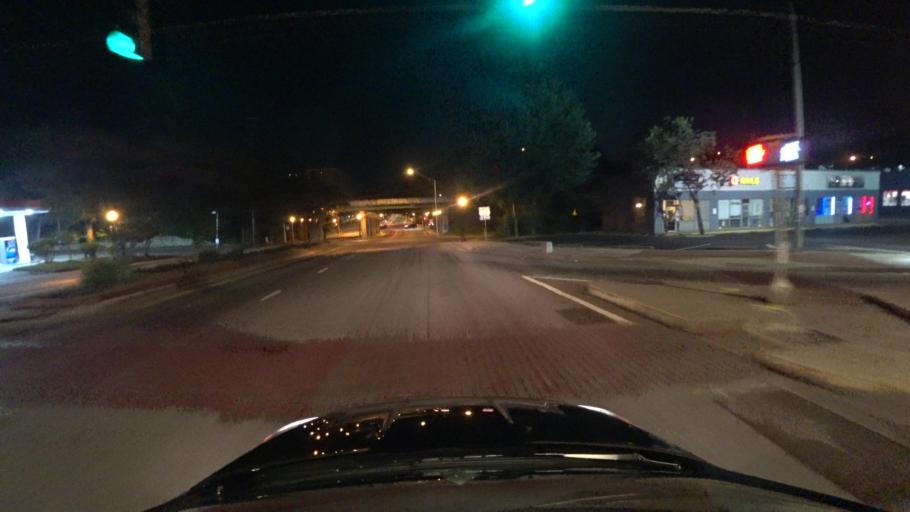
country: US
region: Georgia
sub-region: Fulton County
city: Atlanta
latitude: 33.7405
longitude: -84.4177
